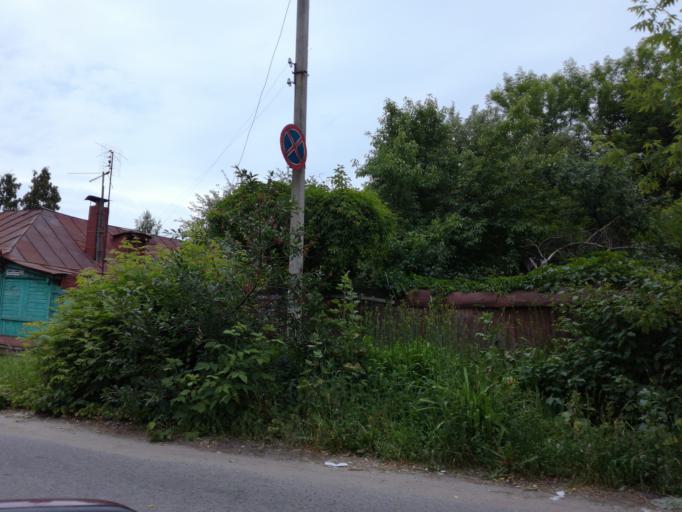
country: RU
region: Kursk
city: Kursk
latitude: 51.7265
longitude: 36.1663
